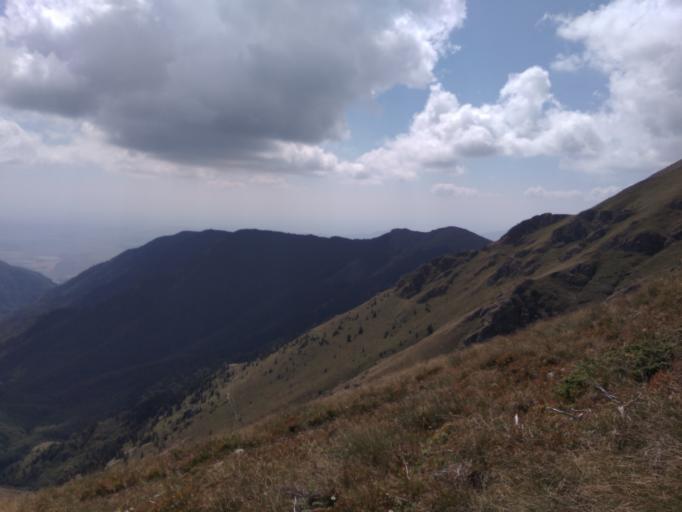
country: BG
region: Plovdiv
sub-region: Obshtina Karlovo
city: Karlovo
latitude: 42.7241
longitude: 24.7936
